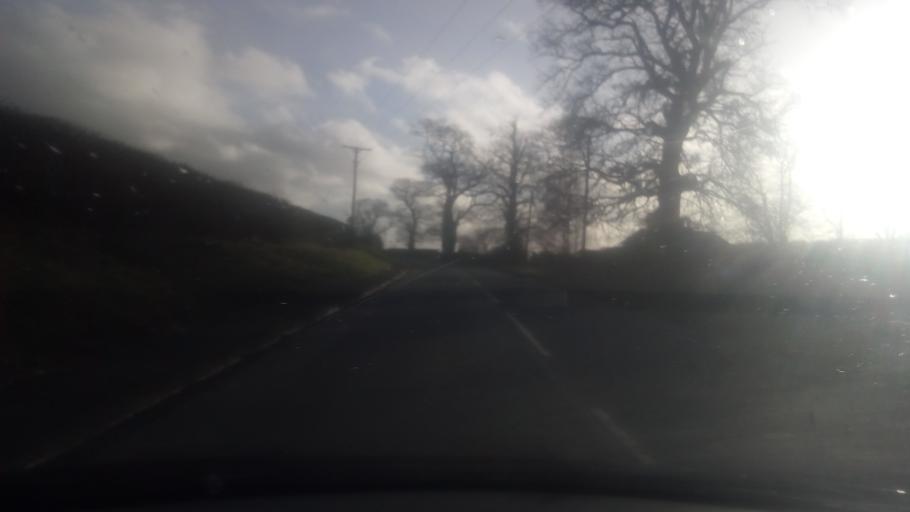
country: GB
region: Scotland
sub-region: The Scottish Borders
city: Kelso
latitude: 55.6207
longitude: -2.4244
